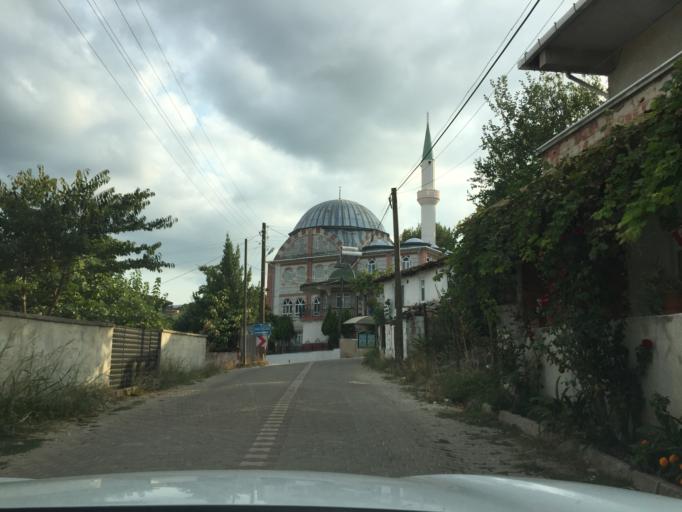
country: TR
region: Balikesir
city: Gonen
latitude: 40.0487
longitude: 27.5835
